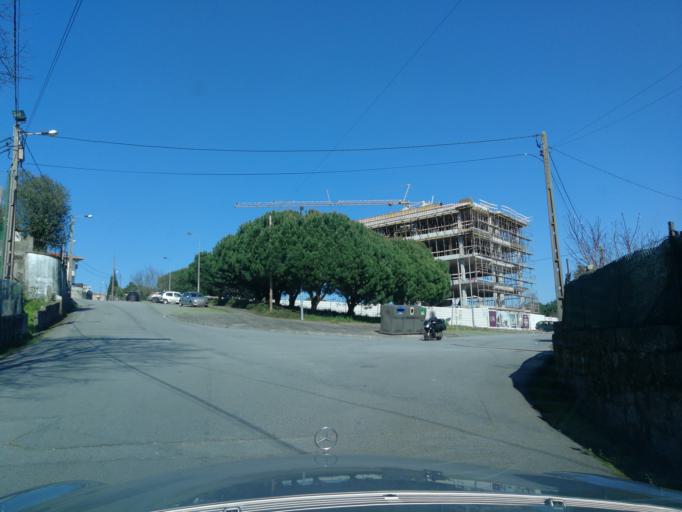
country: PT
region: Braga
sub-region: Vila Nova de Famalicao
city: Calendario
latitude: 41.3973
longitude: -8.5267
